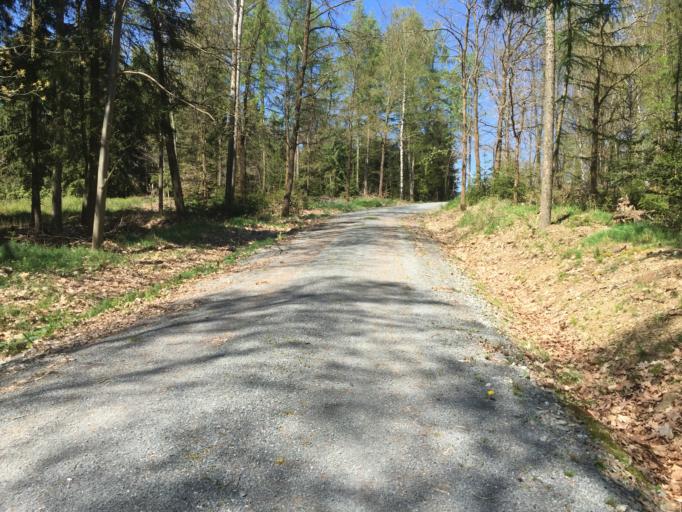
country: DE
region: Saxony
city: Neuensalz
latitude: 50.5097
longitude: 12.1925
